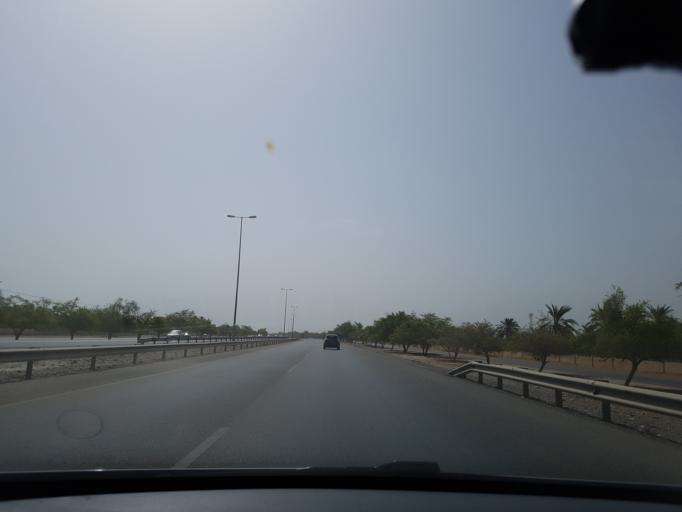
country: OM
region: Al Batinah
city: Al Khaburah
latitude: 23.9455
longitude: 57.1149
